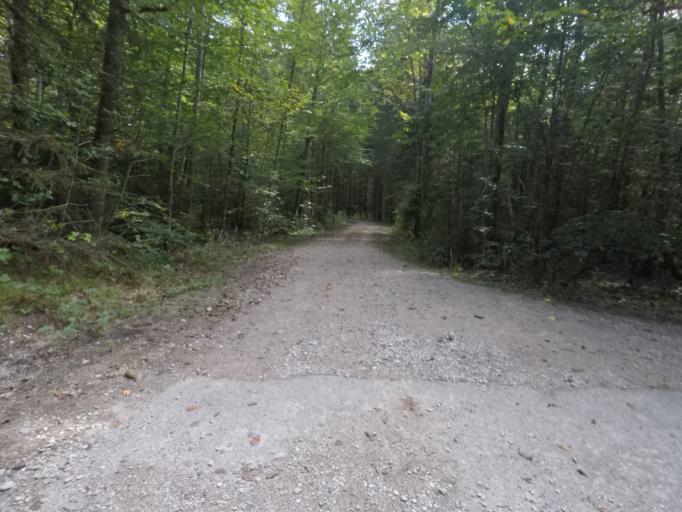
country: DE
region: Bavaria
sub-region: Upper Bavaria
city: Geretsried
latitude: 47.8557
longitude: 11.5090
